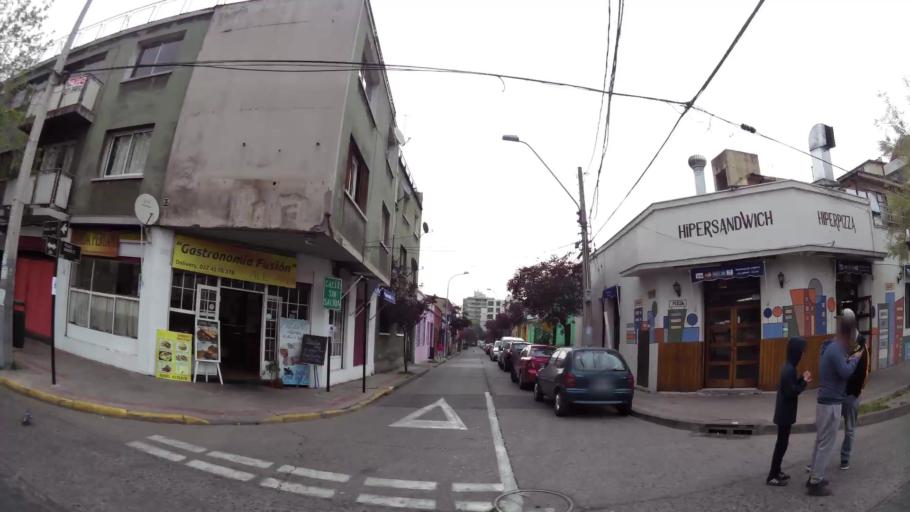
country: CL
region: Santiago Metropolitan
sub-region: Provincia de Santiago
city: Santiago
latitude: -33.4423
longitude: -70.6149
